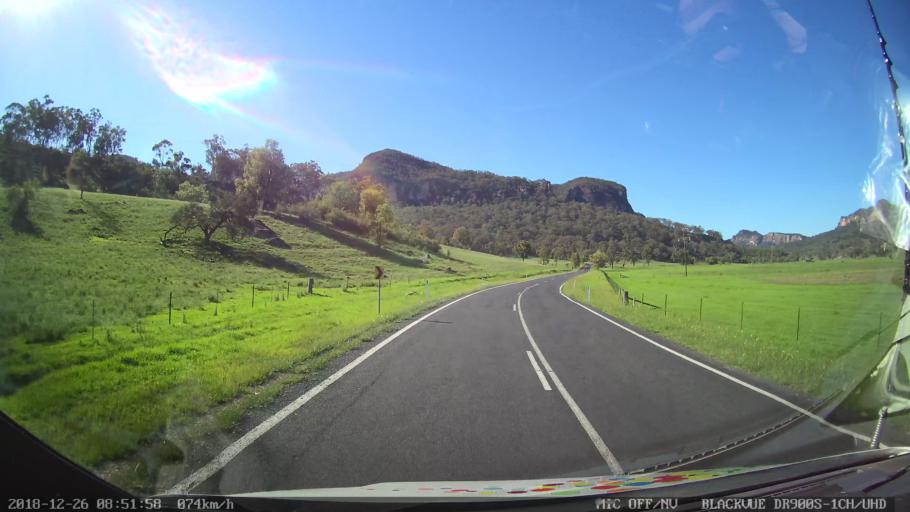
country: AU
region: New South Wales
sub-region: Mid-Western Regional
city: Kandos
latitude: -32.5913
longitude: 150.0879
